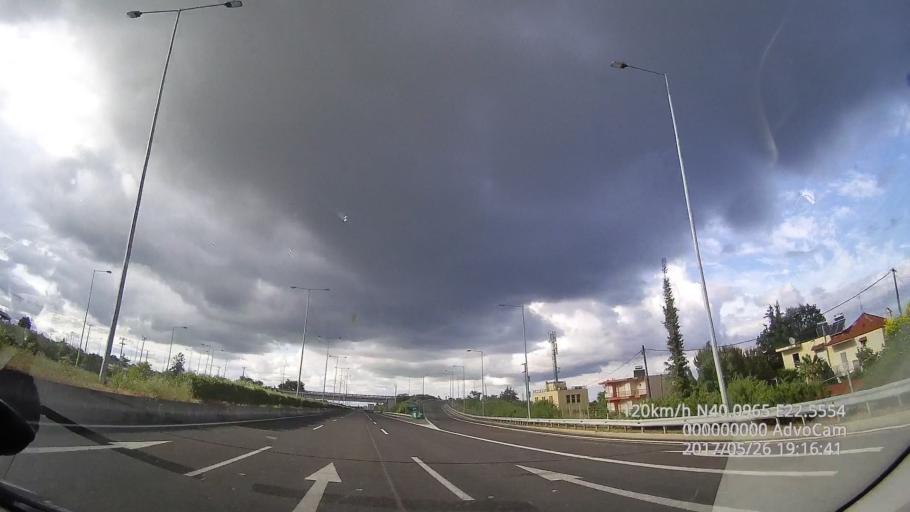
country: GR
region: Central Macedonia
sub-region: Nomos Pierias
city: Aiginio
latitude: 40.4640
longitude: 22.5777
